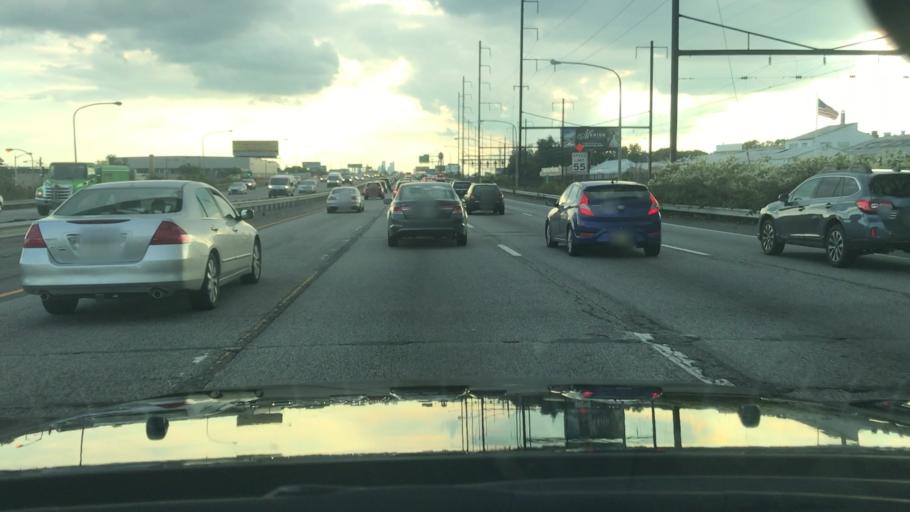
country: US
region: New Jersey
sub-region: Burlington County
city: Palmyra
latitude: 40.0163
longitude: -75.0519
